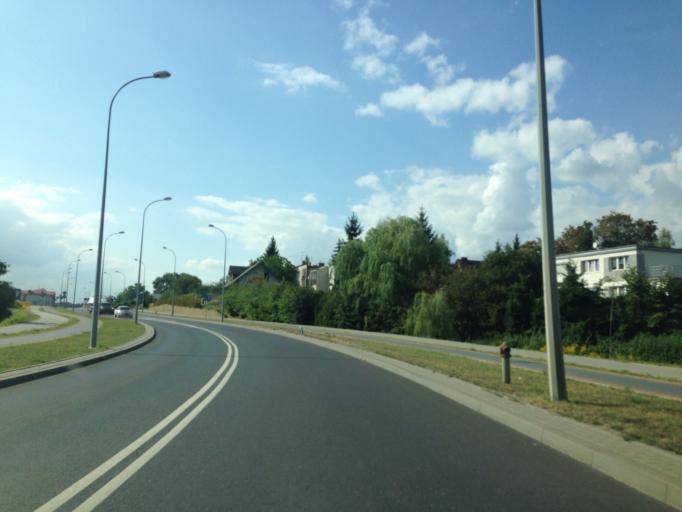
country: PL
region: Warmian-Masurian Voivodeship
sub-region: Powiat ilawski
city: Ilawa
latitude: 53.6008
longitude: 19.5694
